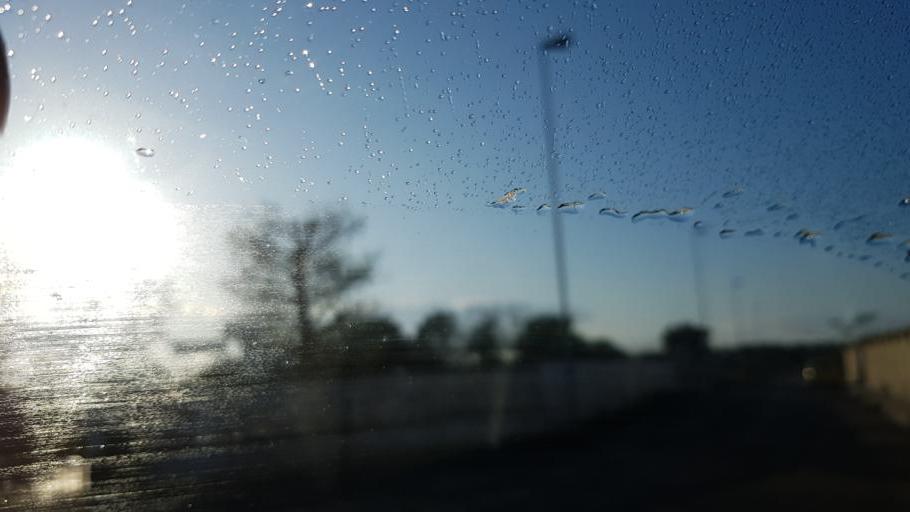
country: IT
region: Apulia
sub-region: Provincia di Brindisi
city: Torchiarolo
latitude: 40.5090
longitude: 18.0918
